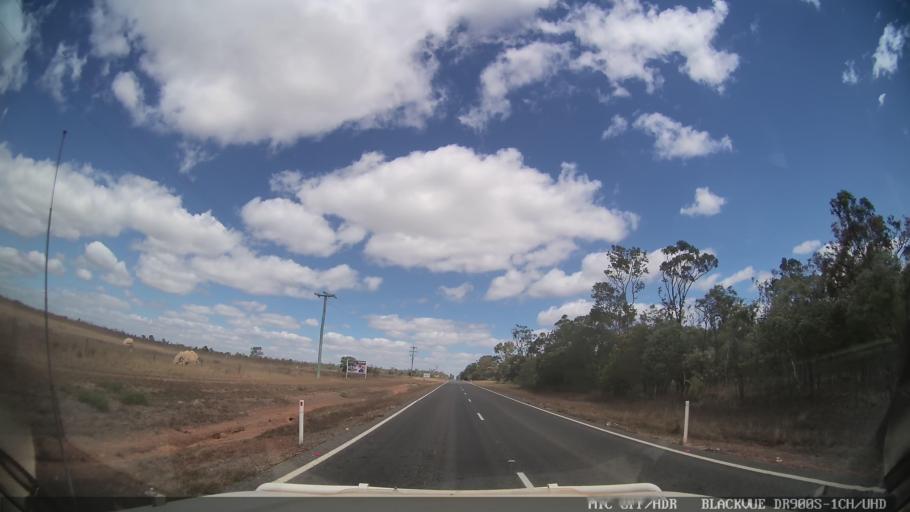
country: AU
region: Queensland
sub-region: Tablelands
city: Ravenshoe
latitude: -18.0382
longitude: 144.8689
